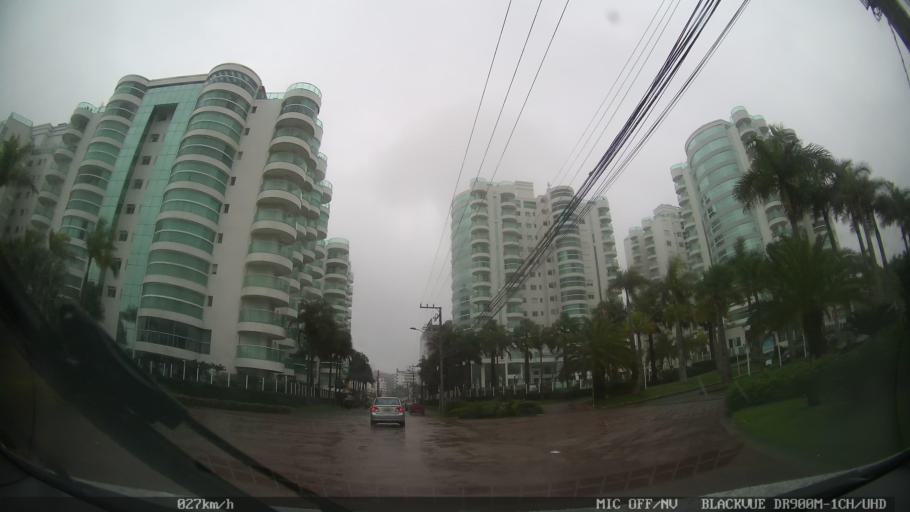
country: BR
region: Santa Catarina
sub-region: Balneario Camboriu
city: Balneario Camboriu
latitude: -26.9520
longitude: -48.6311
